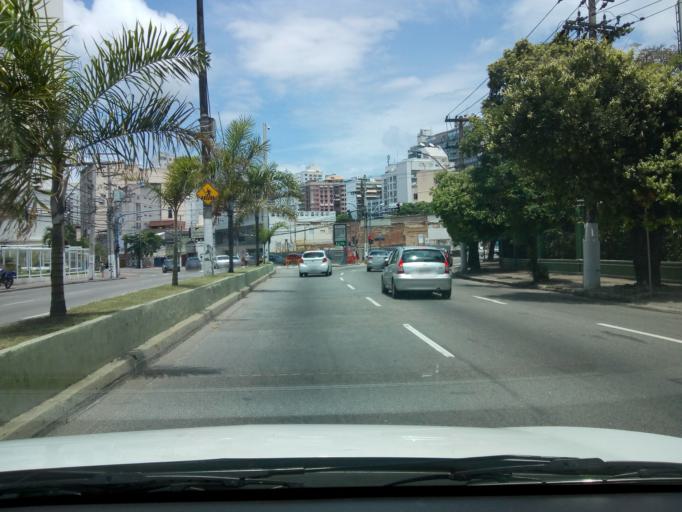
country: BR
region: Rio de Janeiro
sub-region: Niteroi
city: Niteroi
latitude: -22.8980
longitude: -43.1119
